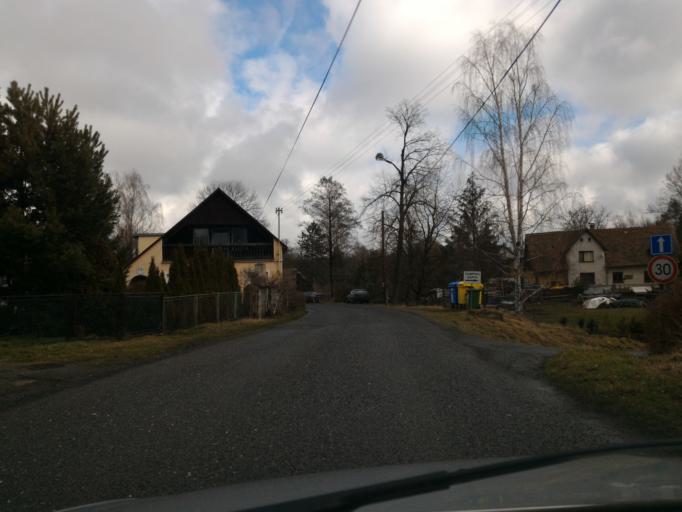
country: CZ
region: Liberecky
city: Visnova
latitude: 50.9245
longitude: 15.0285
